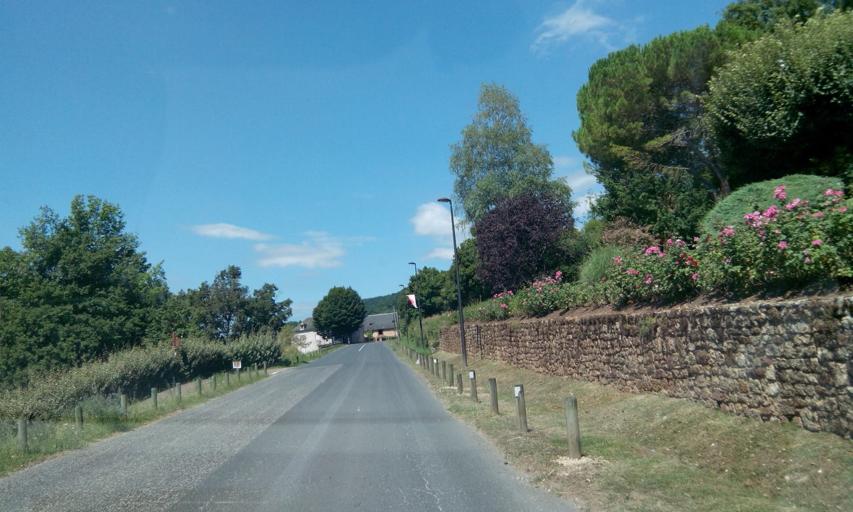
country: FR
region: Limousin
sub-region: Departement de la Correze
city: Meyssac
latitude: 45.0625
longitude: 1.6542
